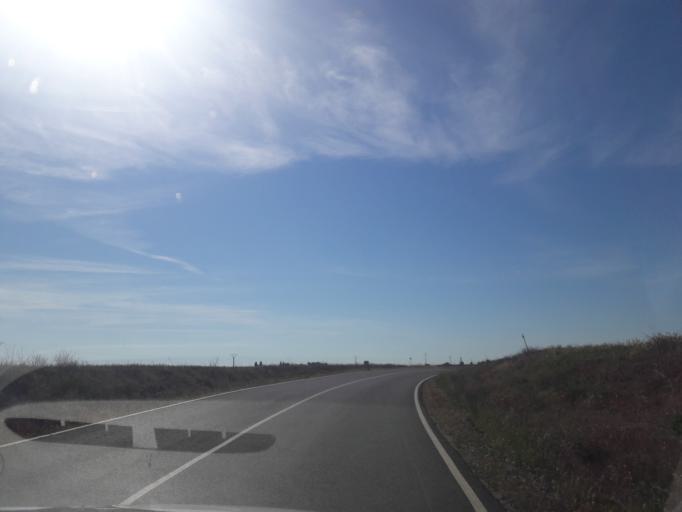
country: ES
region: Castille and Leon
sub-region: Provincia de Salamanca
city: Espino de la Orbada
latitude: 41.0876
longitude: -5.4091
